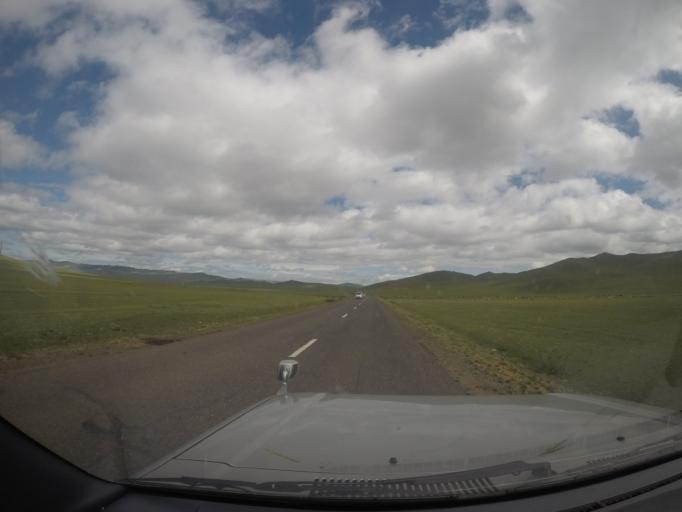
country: MN
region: Hentiy
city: Modot
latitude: 47.7632
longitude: 108.9082
